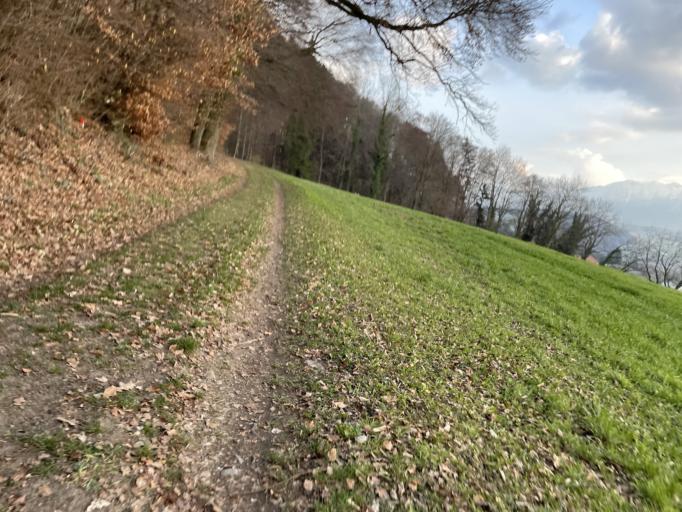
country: CH
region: Bern
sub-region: Bern-Mittelland District
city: Muhlethurnen
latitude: 46.8406
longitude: 7.5260
